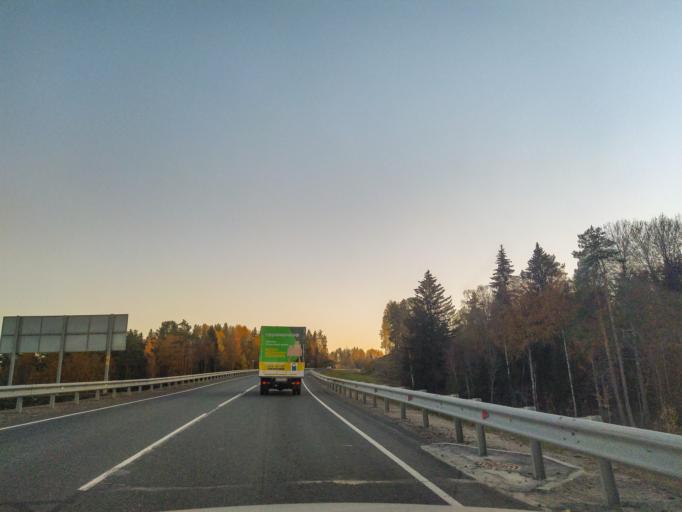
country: RU
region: Leningrad
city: Kuznechnoye
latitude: 61.3017
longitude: 29.7856
